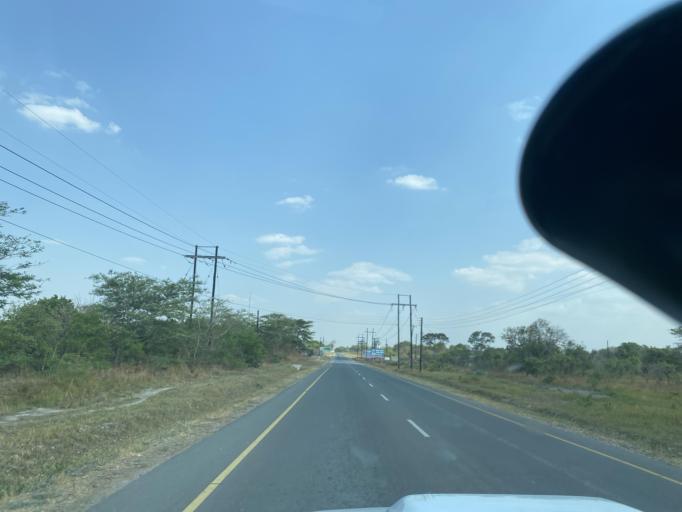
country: ZM
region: Lusaka
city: Lusaka
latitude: -15.3348
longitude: 28.0729
